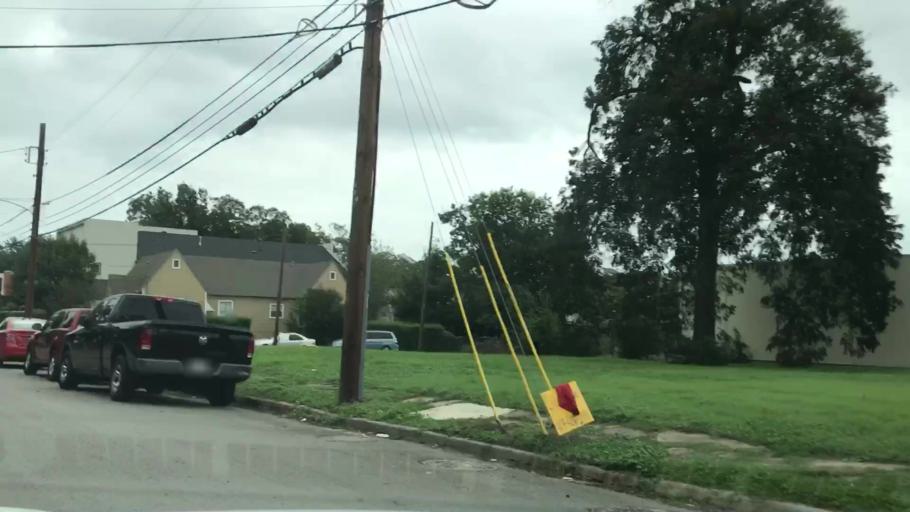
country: US
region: Texas
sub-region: Dallas County
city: Dallas
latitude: 32.8014
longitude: -96.7854
